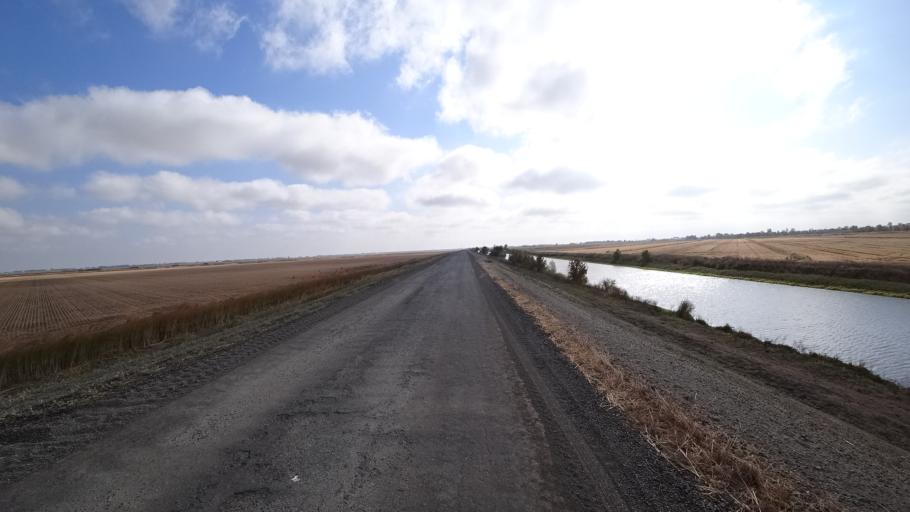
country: US
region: California
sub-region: Yolo County
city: Woodland
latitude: 38.8214
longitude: -121.7934
